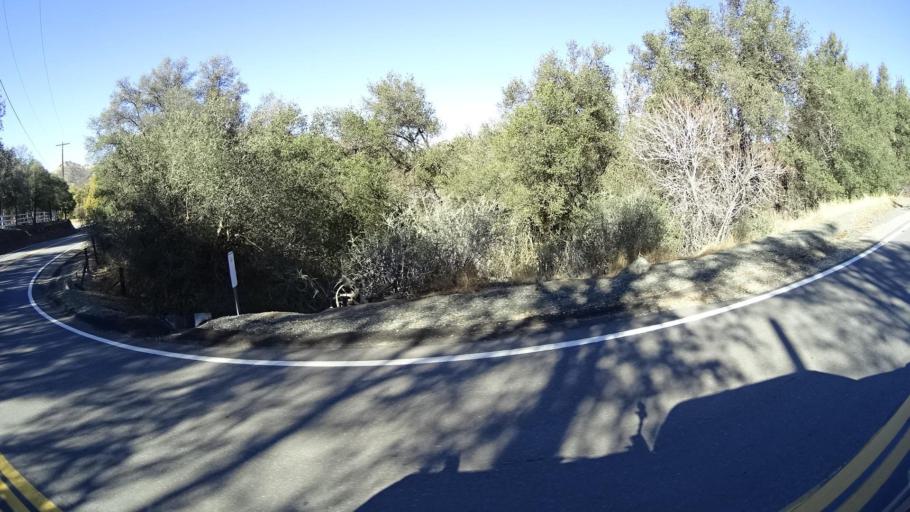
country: US
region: California
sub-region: Kern County
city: Alta Sierra
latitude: 35.7360
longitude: -118.6579
